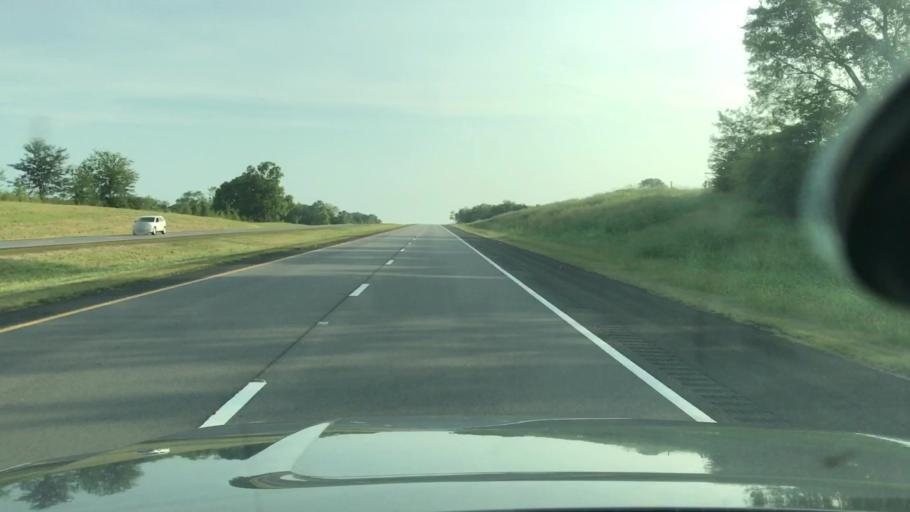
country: US
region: Tennessee
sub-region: Sumner County
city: Gallatin
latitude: 36.4221
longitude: -86.4662
